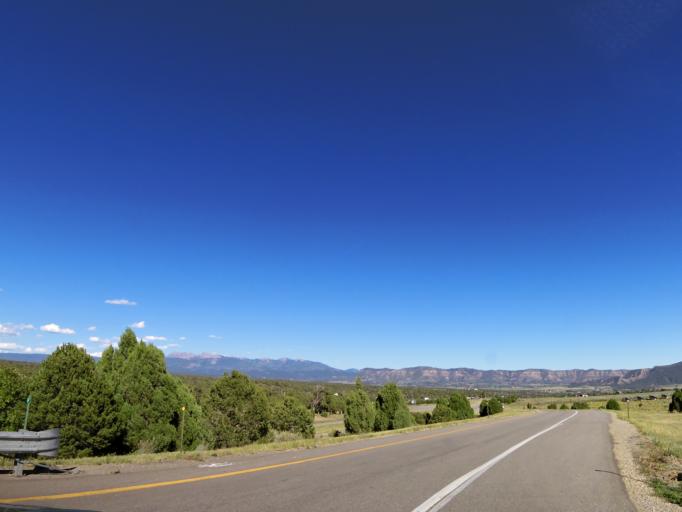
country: US
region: Colorado
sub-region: Montezuma County
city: Mancos
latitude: 37.3401
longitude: -108.4116
